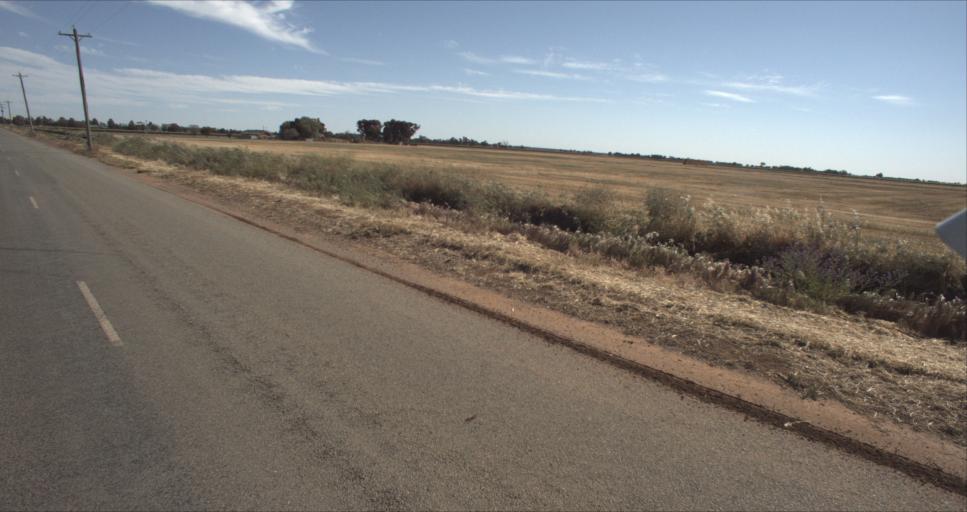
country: AU
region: New South Wales
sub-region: Leeton
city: Leeton
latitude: -34.5744
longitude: 146.3811
